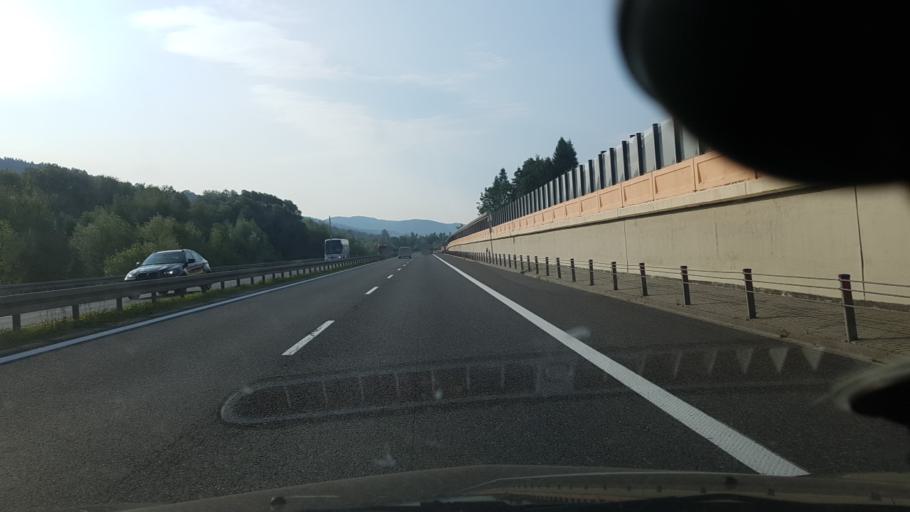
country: PL
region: Lesser Poland Voivodeship
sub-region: Powiat myslenicki
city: Pcim
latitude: 49.7793
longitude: 19.9543
